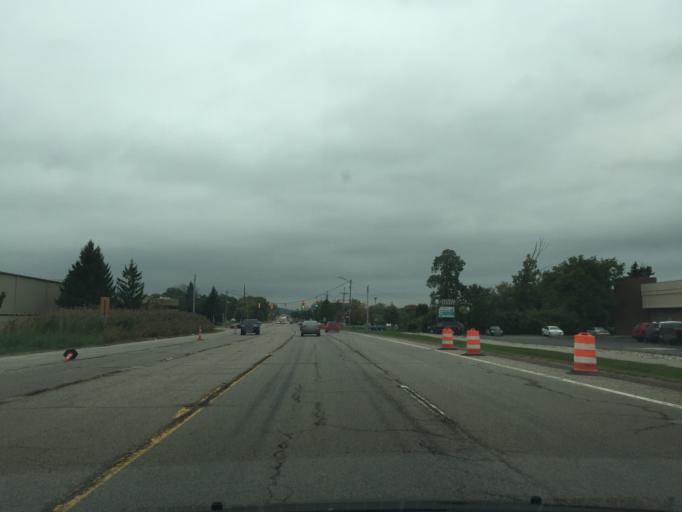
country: US
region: Michigan
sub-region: Oakland County
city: Auburn Hills
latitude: 42.6569
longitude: -83.2457
